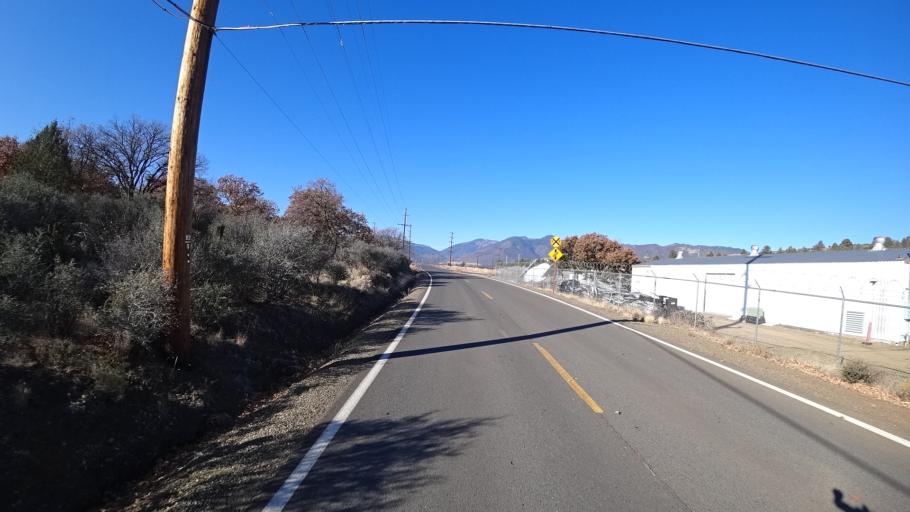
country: US
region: California
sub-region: Siskiyou County
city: Yreka
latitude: 41.7391
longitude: -122.6134
